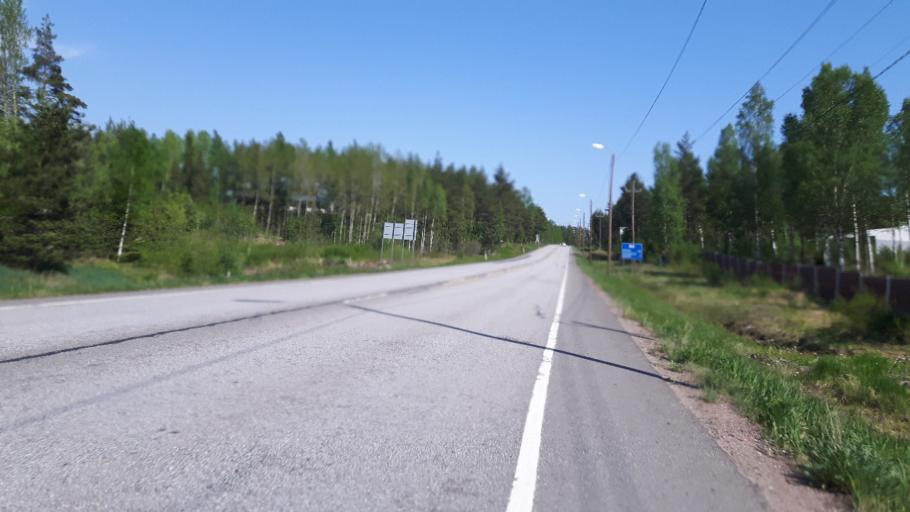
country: FI
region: Kymenlaakso
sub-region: Kotka-Hamina
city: Broby
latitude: 60.4890
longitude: 26.6695
